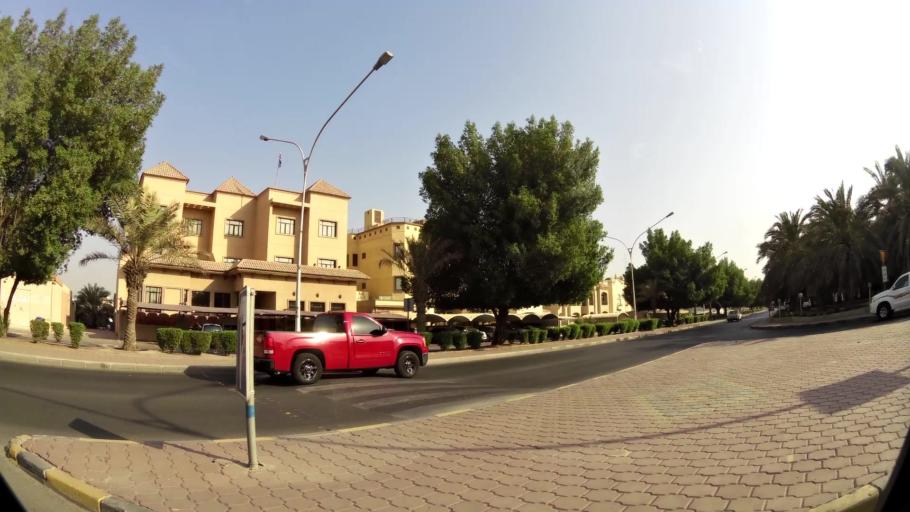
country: KW
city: Bayan
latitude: 29.3172
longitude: 48.0384
